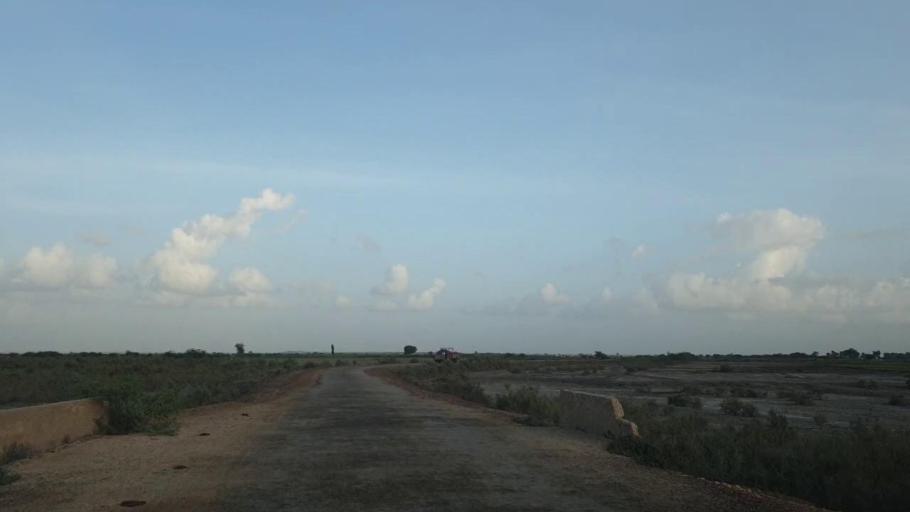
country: PK
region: Sindh
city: Kadhan
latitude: 24.5644
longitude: 69.1211
